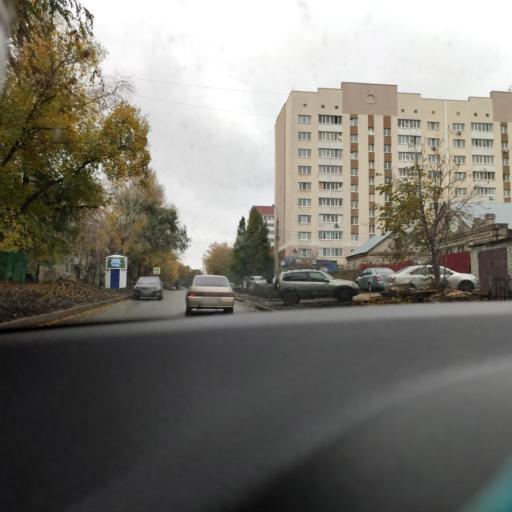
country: RU
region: Samara
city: Samara
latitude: 53.2208
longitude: 50.2232
